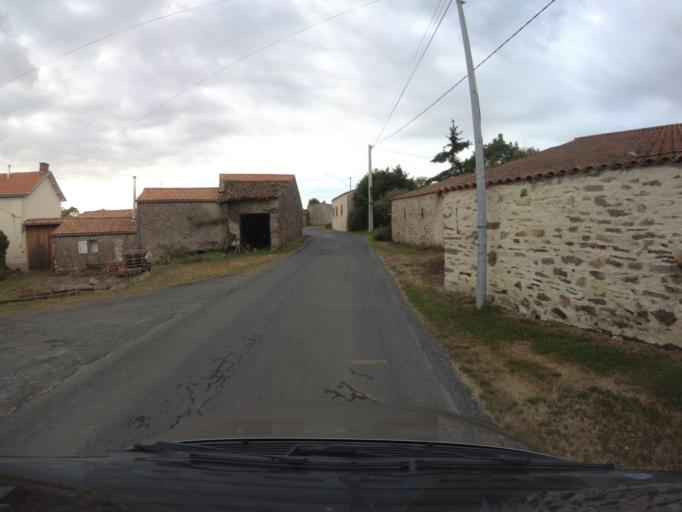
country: FR
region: Pays de la Loire
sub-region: Departement de la Vendee
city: Saint-Hilaire-de-Loulay
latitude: 47.0259
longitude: -1.3217
